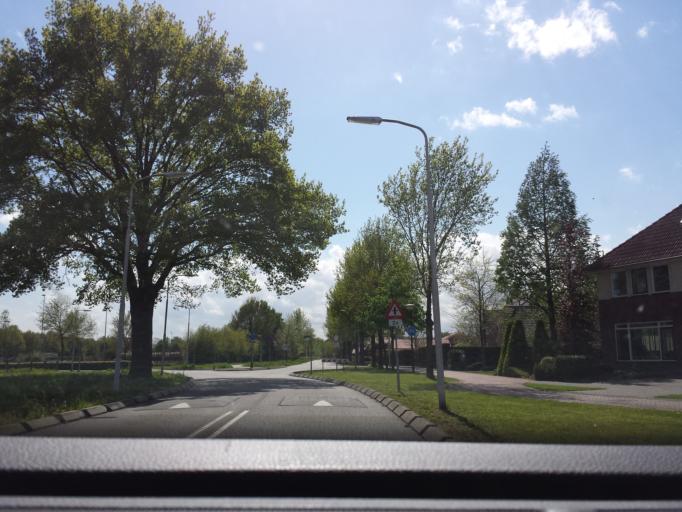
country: NL
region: Gelderland
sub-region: Gemeente Lochem
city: Barchem
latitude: 52.0882
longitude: 6.4569
